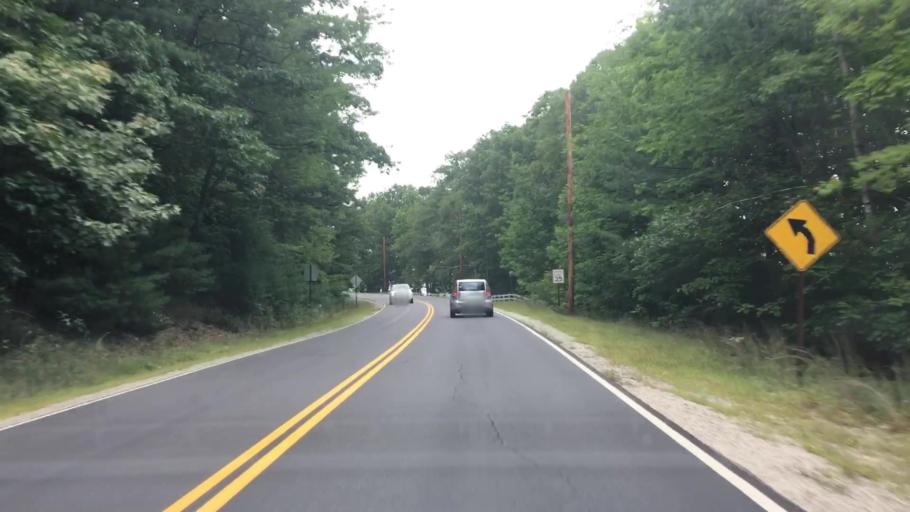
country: US
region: Maine
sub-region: Cumberland County
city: New Gloucester
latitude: 43.8907
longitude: -70.2531
